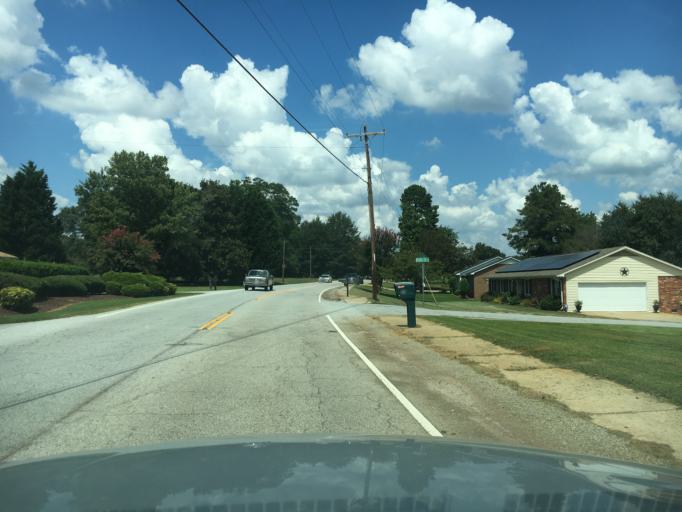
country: US
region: South Carolina
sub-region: Spartanburg County
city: Fairforest
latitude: 34.9123
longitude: -82.0053
